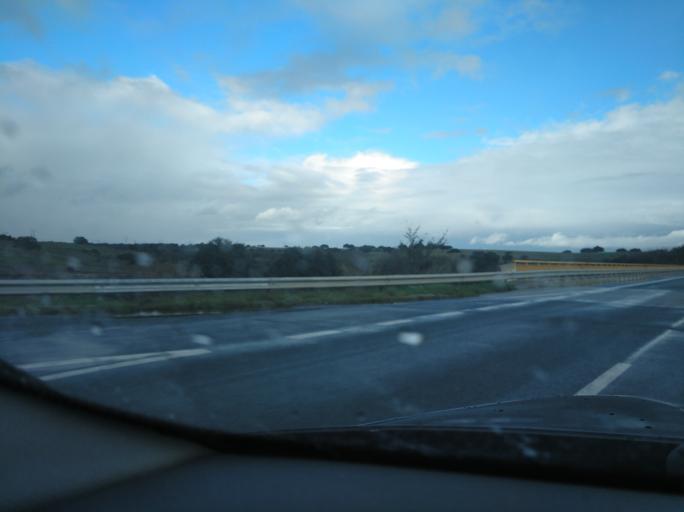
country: PT
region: Setubal
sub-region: Grandola
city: Grandola
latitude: 38.0118
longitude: -8.3854
